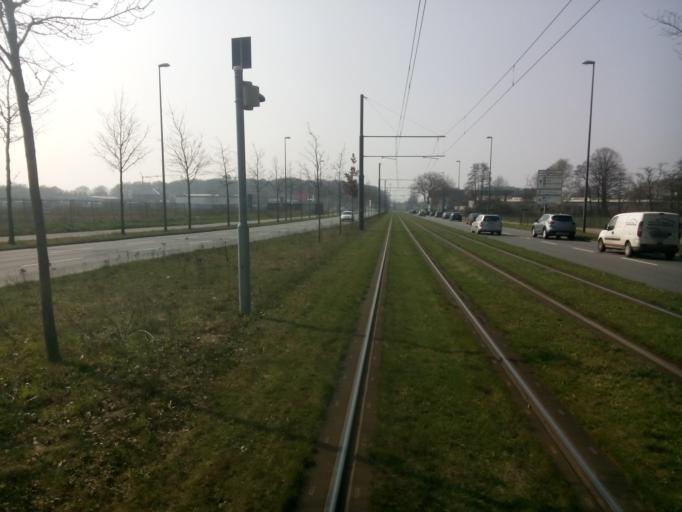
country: DE
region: Lower Saxony
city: Oyten
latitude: 53.0563
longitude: 8.9631
